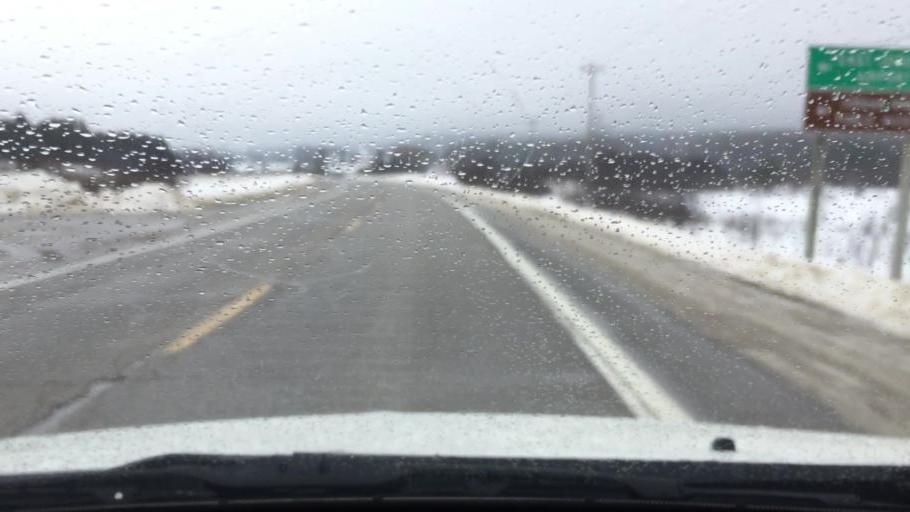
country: US
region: Michigan
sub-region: Charlevoix County
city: East Jordan
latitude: 45.1337
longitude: -85.1397
